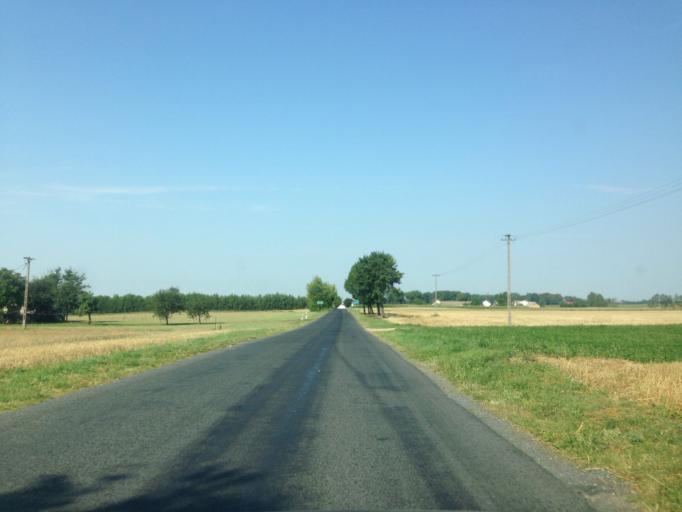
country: PL
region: Kujawsko-Pomorskie
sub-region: Powiat brodnicki
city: Swiedziebnia
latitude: 53.1688
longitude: 19.5997
